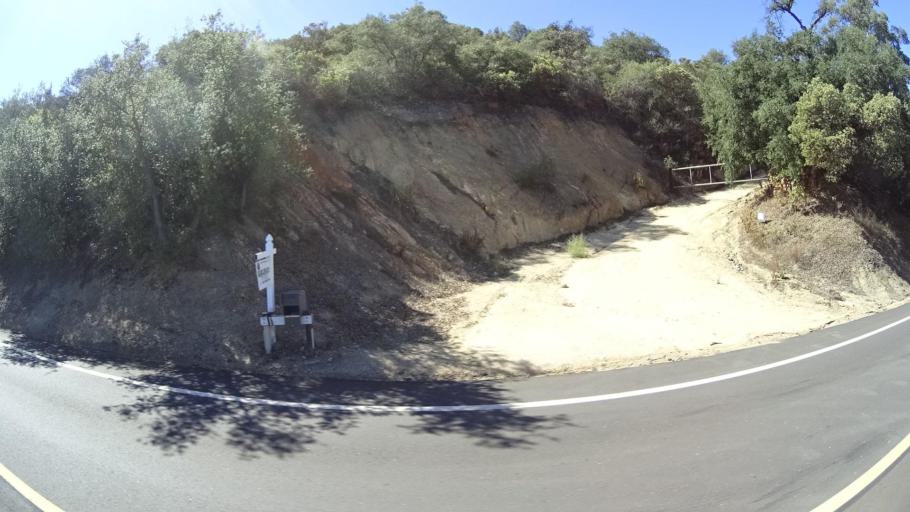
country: US
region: California
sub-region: San Diego County
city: Jamul
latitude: 32.7293
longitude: -116.7836
